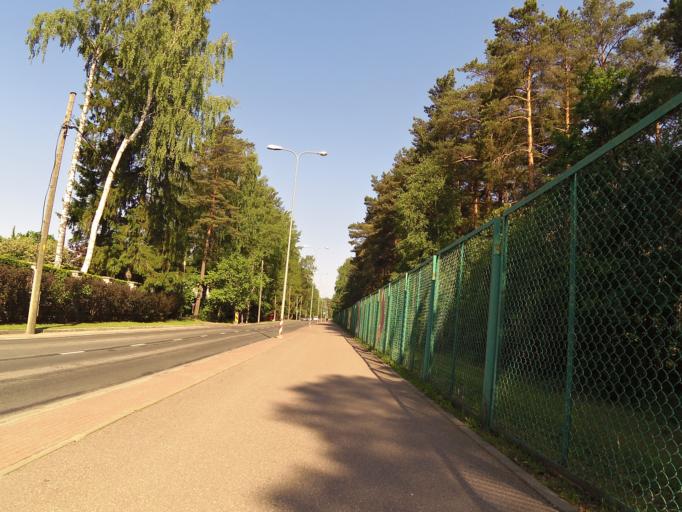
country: EE
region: Harju
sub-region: Saue vald
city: Laagri
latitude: 59.4315
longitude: 24.6362
